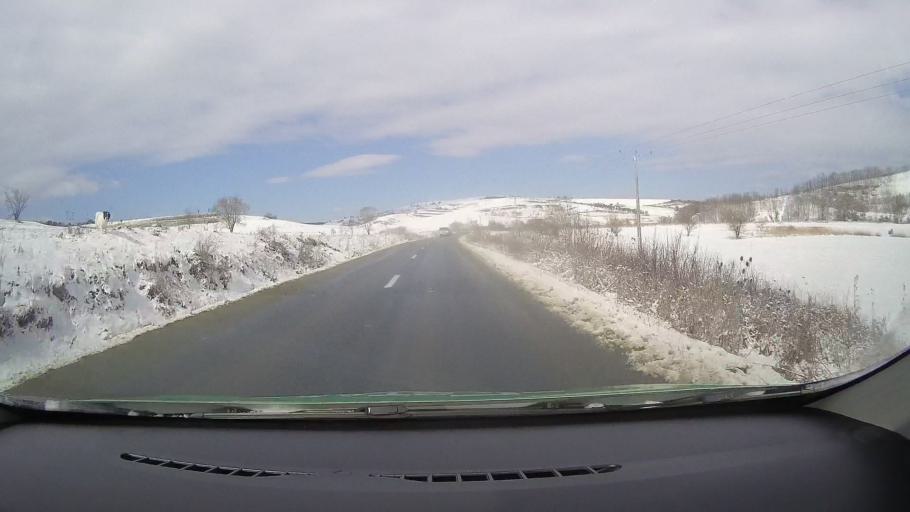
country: RO
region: Sibiu
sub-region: Comuna Altina
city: Altina
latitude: 45.9719
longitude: 24.4665
